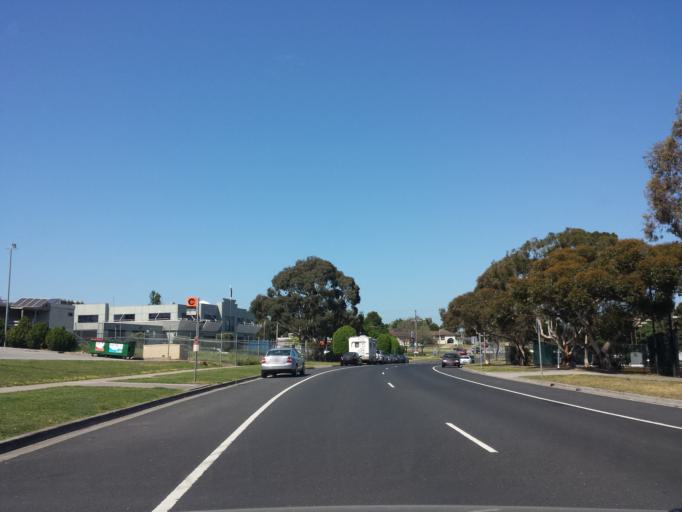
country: AU
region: Victoria
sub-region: Casey
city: Narre Warren
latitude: -38.0248
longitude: 145.3106
